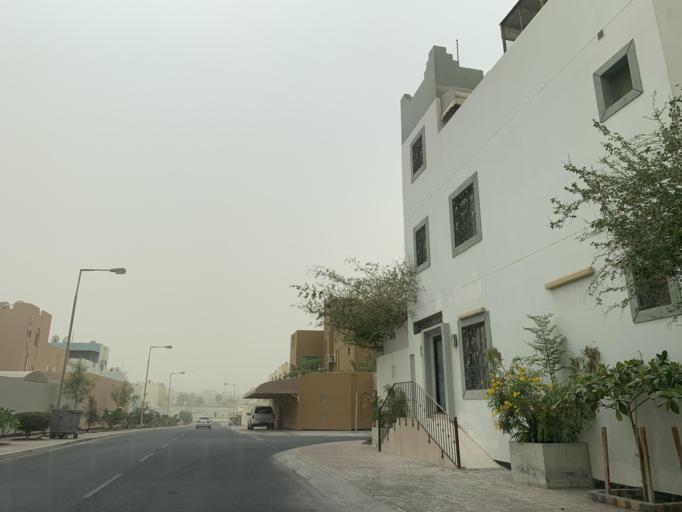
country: BH
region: Central Governorate
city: Madinat Hamad
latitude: 26.1362
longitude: 50.5135
